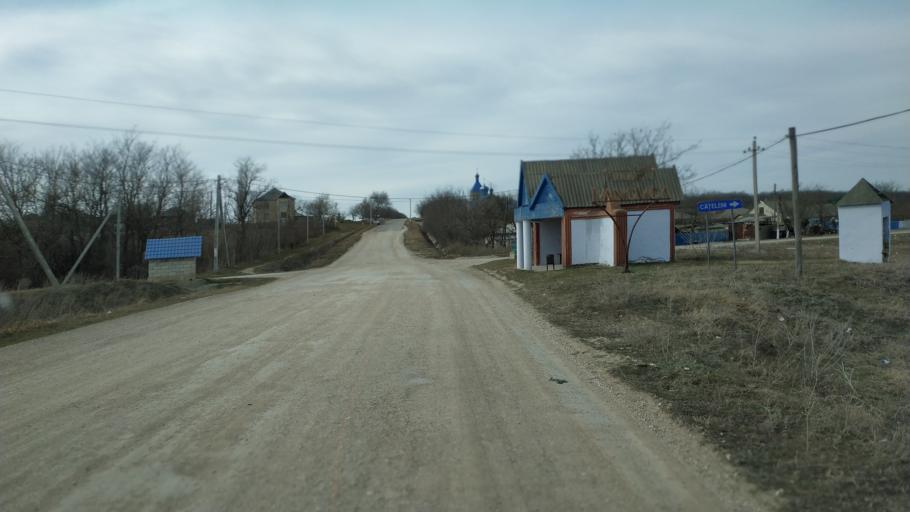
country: RO
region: Vaslui
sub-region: Comuna Dranceni
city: Dranceni
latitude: 46.8600
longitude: 28.2026
